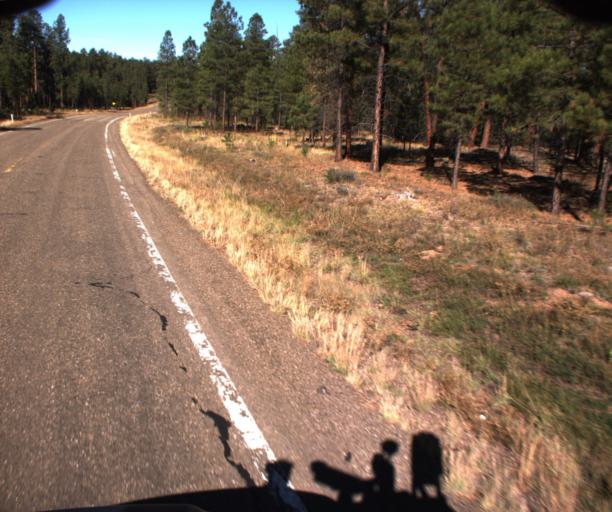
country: US
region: Arizona
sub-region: Coconino County
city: Fredonia
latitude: 36.7443
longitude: -112.2412
